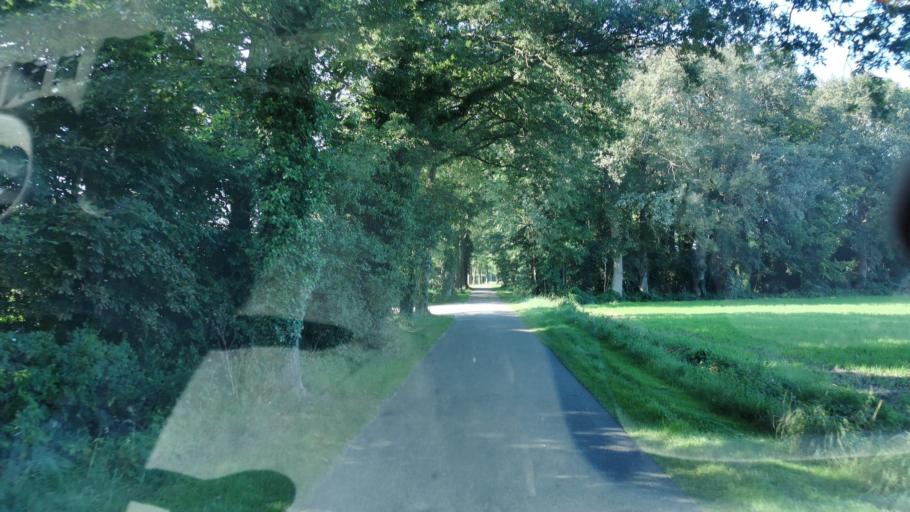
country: DE
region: Lower Saxony
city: Lage
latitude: 52.4178
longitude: 6.9481
